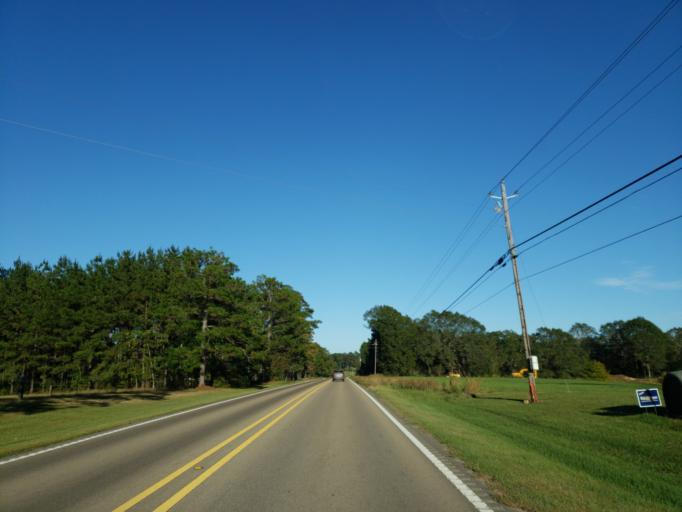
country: US
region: Mississippi
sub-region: Perry County
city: Richton
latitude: 31.3660
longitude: -88.8817
